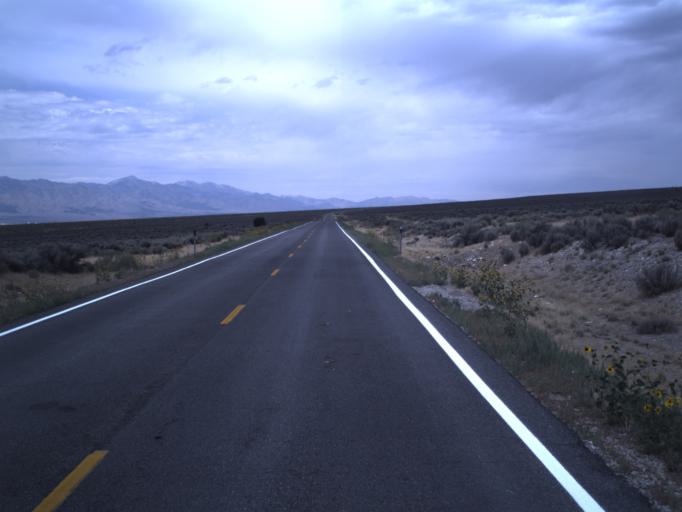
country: US
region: Utah
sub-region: Utah County
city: Eagle Mountain
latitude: 40.2803
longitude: -112.2571
